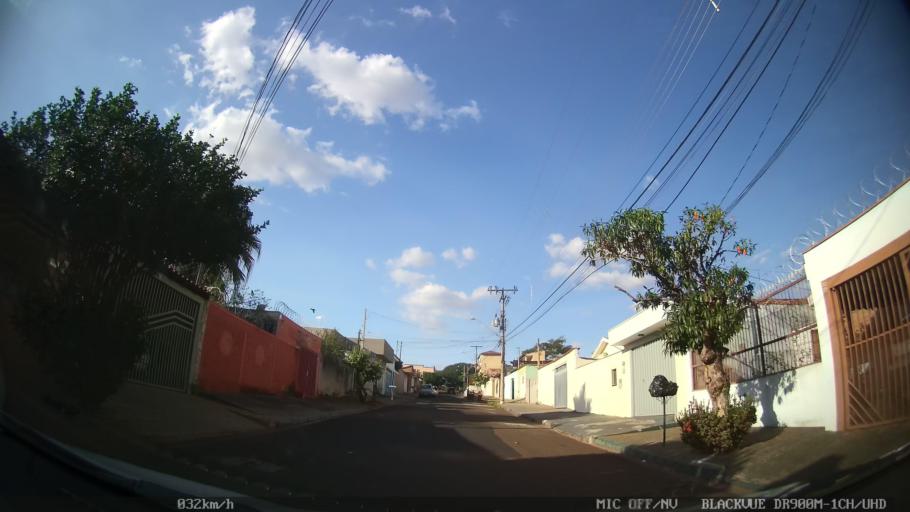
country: BR
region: Sao Paulo
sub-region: Ribeirao Preto
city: Ribeirao Preto
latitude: -21.1889
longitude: -47.7867
